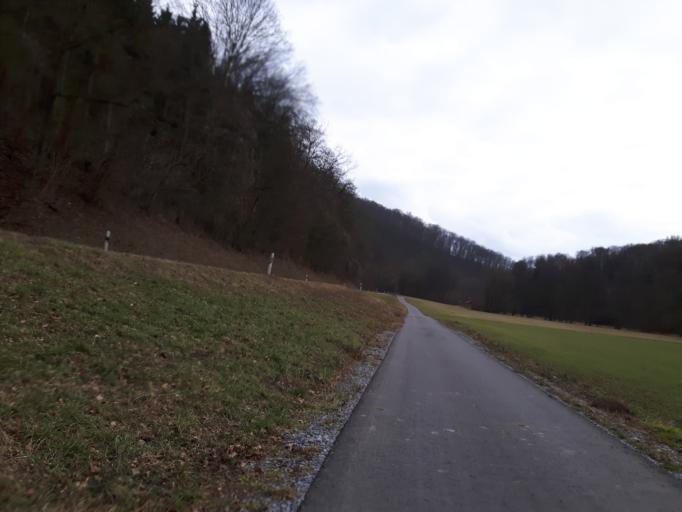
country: DE
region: Baden-Wuerttemberg
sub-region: Regierungsbezirk Stuttgart
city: Zweiflingen
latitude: 49.2426
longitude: 9.4609
